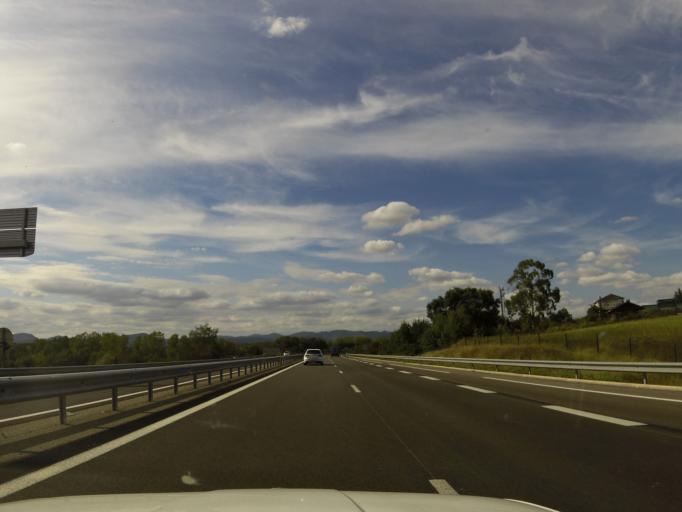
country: FR
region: Languedoc-Roussillon
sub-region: Departement du Gard
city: Saint-Hilaire-de-Brethmas
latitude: 44.0656
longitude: 4.1174
